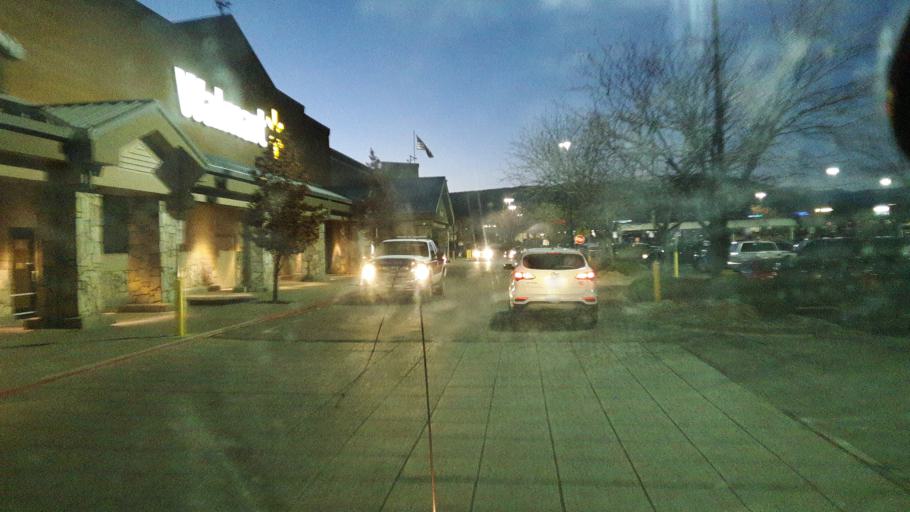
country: US
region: Colorado
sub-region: La Plata County
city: Durango
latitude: 37.2302
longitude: -107.8650
